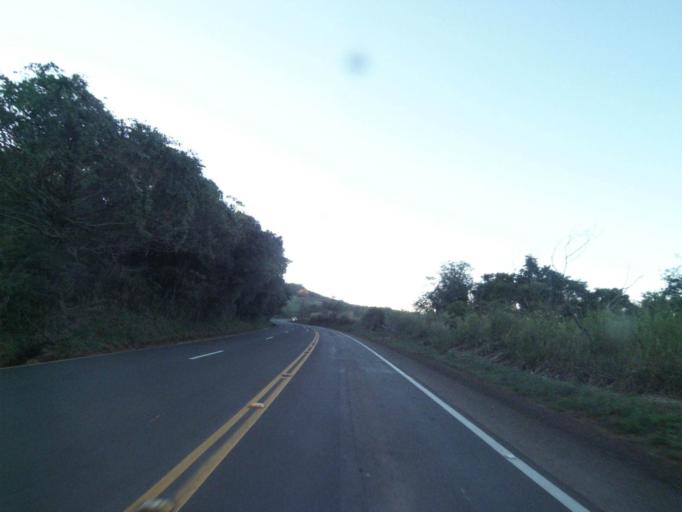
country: BR
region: Parana
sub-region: Apucarana
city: Apucarana
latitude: -23.6791
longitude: -51.1188
